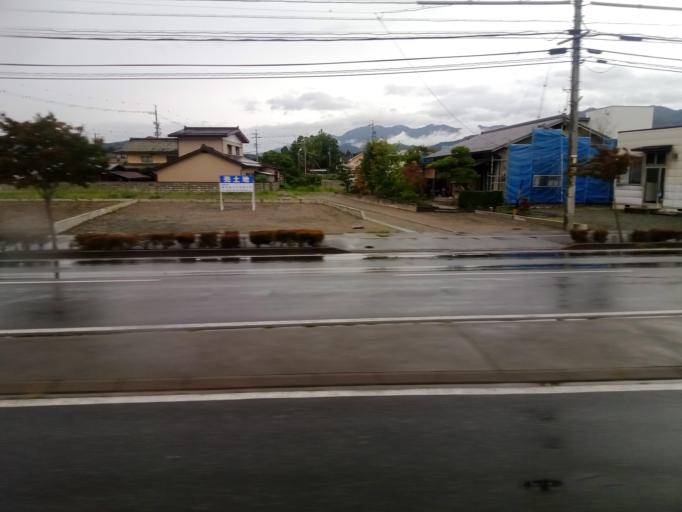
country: JP
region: Nagano
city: Nagano-shi
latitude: 36.6091
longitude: 138.1792
